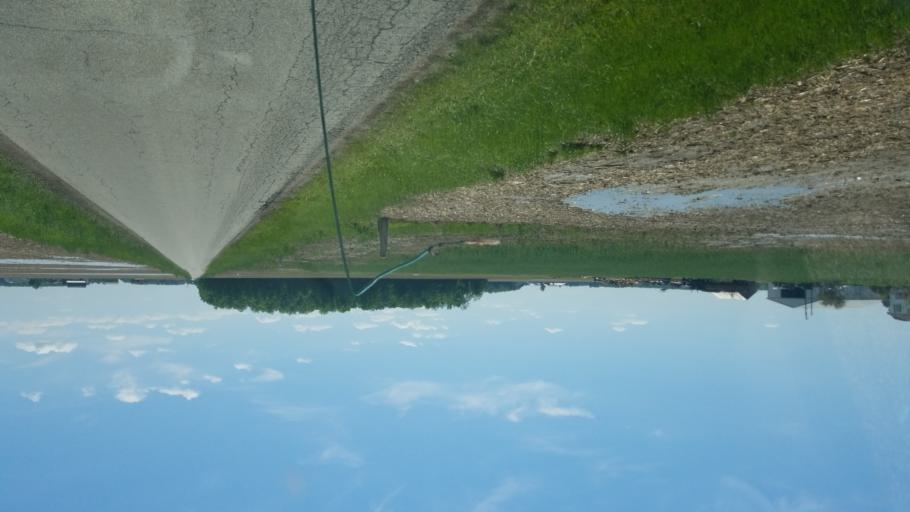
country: US
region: Ohio
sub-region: Crawford County
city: Bucyrus
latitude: 40.9795
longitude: -82.9999
